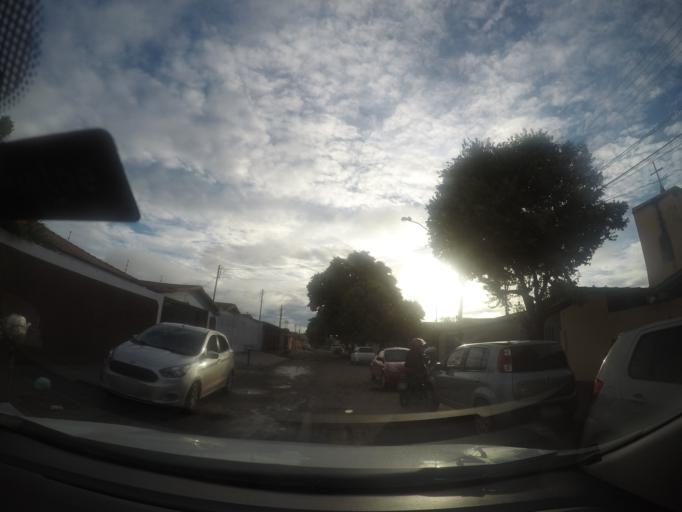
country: BR
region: Goias
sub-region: Goiania
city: Goiania
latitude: -16.6859
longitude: -49.3117
